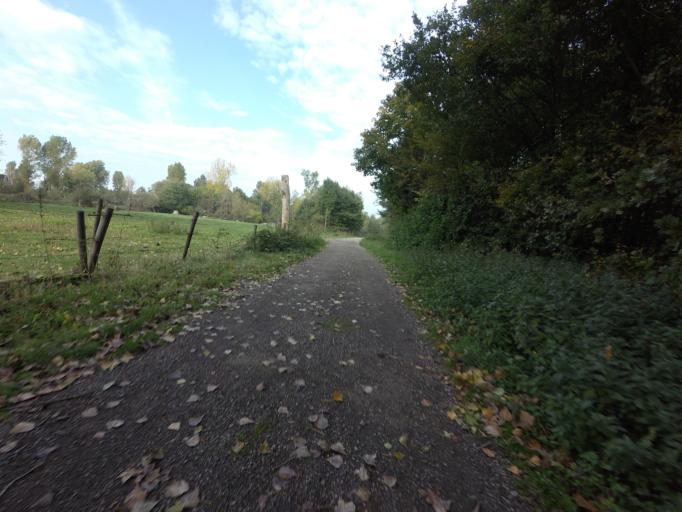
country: DE
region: North Rhine-Westphalia
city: Julich
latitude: 50.9408
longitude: 6.3398
